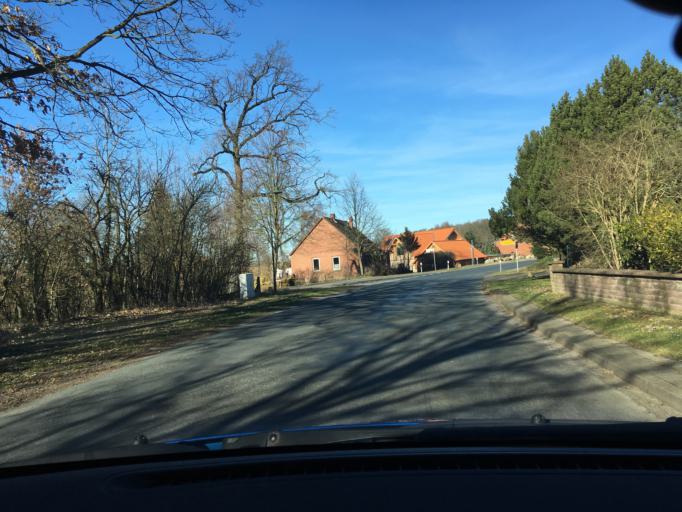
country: DE
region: Lower Saxony
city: Schwienau
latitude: 52.9804
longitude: 10.4446
